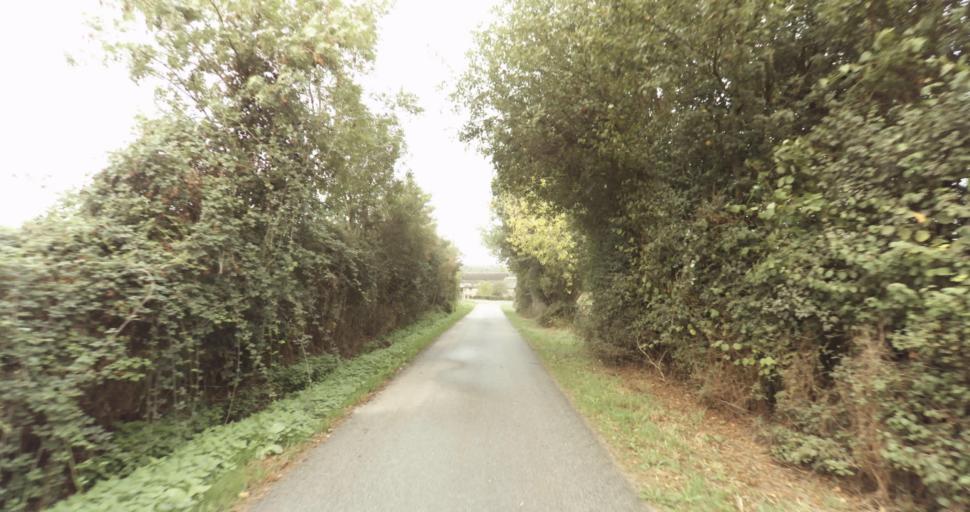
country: FR
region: Lower Normandy
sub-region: Departement de l'Orne
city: Sainte-Gauburge-Sainte-Colombe
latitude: 48.7445
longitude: 0.4521
